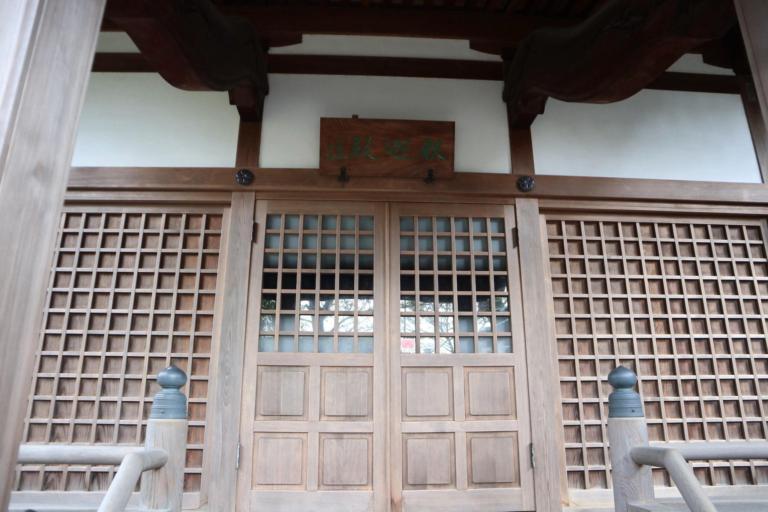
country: JP
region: Tokyo
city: Urayasu
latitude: 35.6767
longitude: 139.8799
